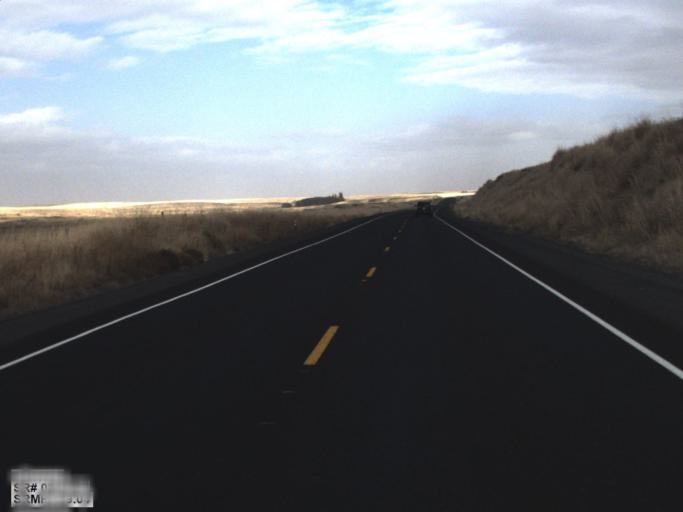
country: US
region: Washington
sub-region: Lincoln County
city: Davenport
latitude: 47.4957
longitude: -118.2418
